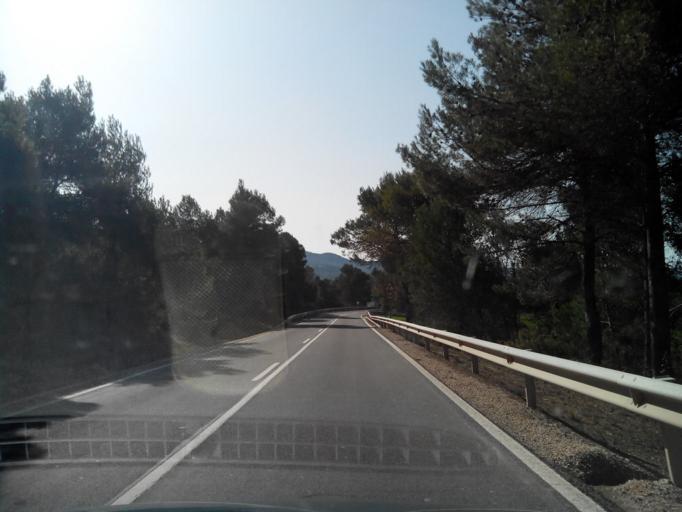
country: ES
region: Catalonia
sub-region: Provincia de Tarragona
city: Conesa
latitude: 41.4918
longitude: 1.3185
